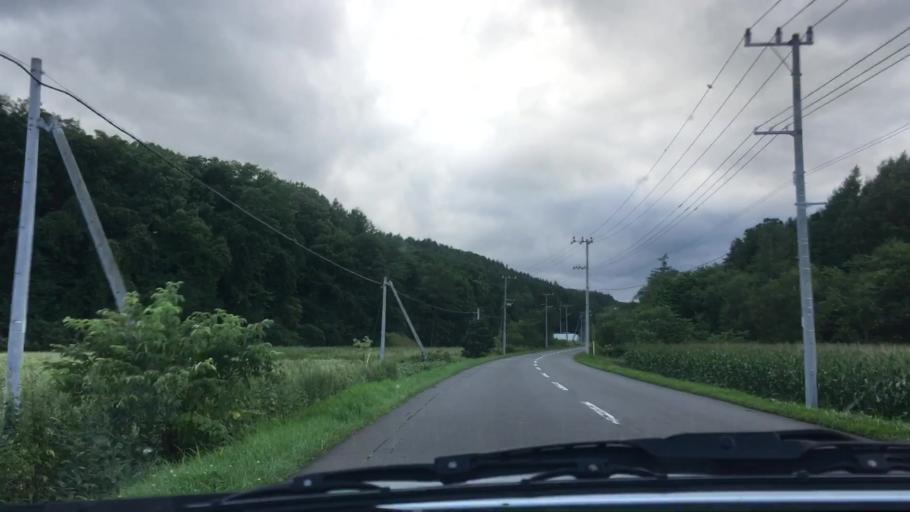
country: JP
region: Hokkaido
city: Otofuke
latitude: 43.1417
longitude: 142.8846
